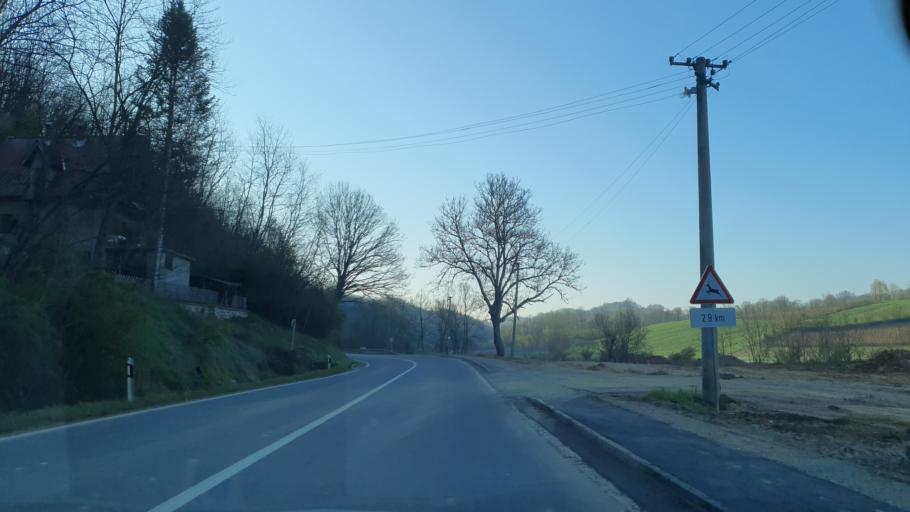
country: RS
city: Bukor
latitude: 44.4498
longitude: 19.4975
